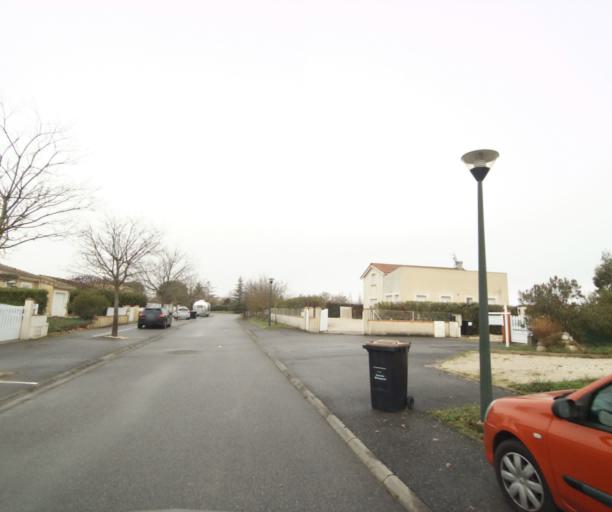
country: FR
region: Midi-Pyrenees
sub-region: Departement de la Haute-Garonne
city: Villemur-sur-Tarn
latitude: 43.8565
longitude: 1.4823
